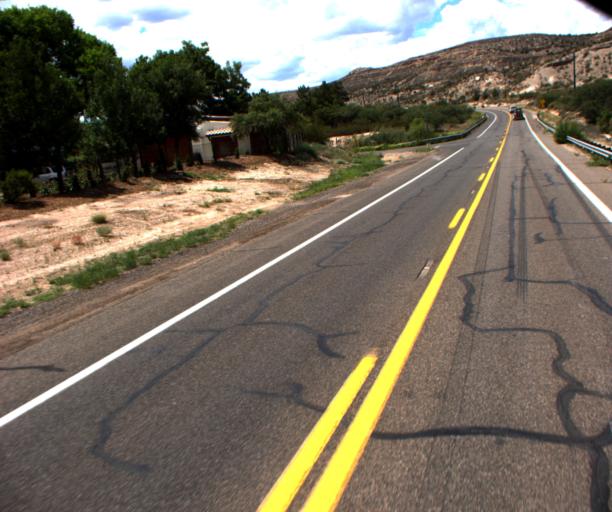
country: US
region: Arizona
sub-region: Yavapai County
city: Camp Verde
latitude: 34.5292
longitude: -111.7832
